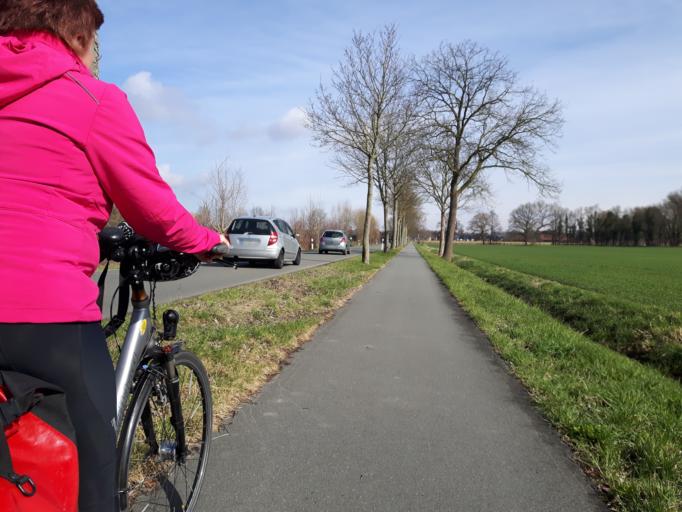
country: DE
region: North Rhine-Westphalia
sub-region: Regierungsbezirk Munster
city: Dulmen
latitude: 51.8111
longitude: 7.2696
